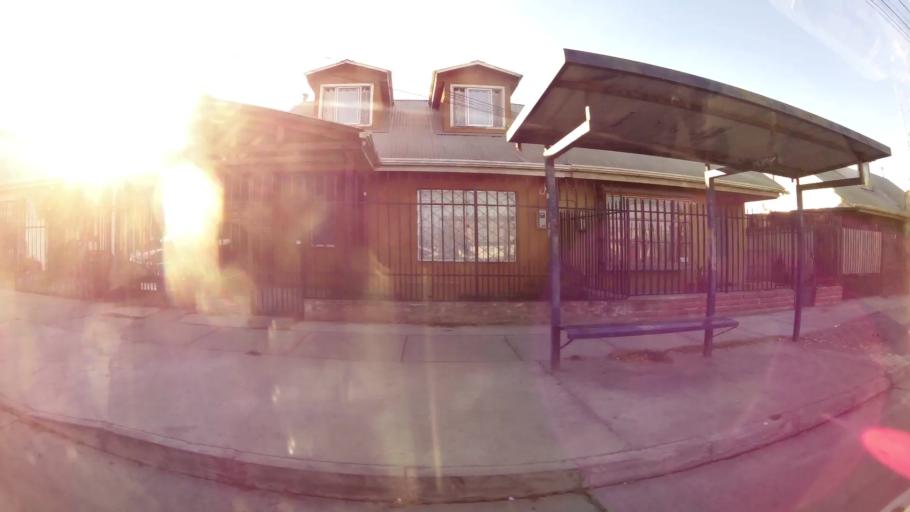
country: CL
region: O'Higgins
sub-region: Provincia de Cachapoal
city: Rancagua
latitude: -34.1767
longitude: -70.7655
